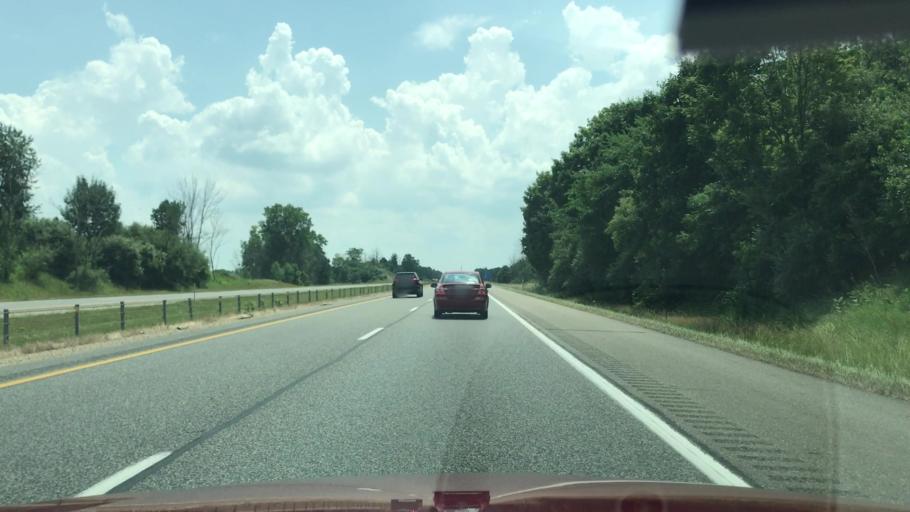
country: US
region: Michigan
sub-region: Allegan County
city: Otsego
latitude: 42.5634
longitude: -85.6626
